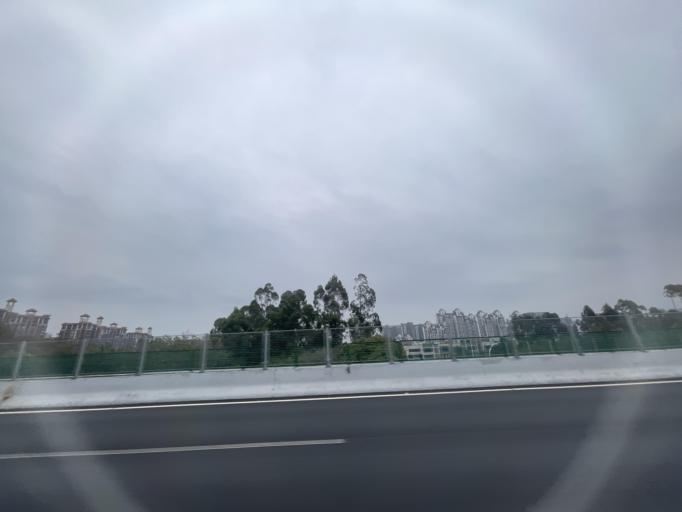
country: CN
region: Guangdong
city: Huangge
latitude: 22.7882
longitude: 113.5208
